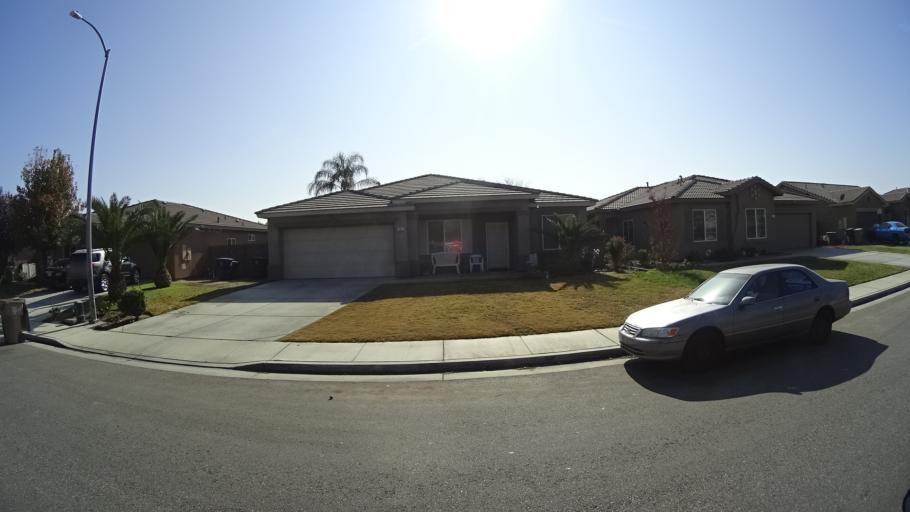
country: US
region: California
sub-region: Kern County
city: Greenfield
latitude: 35.2806
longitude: -119.0142
